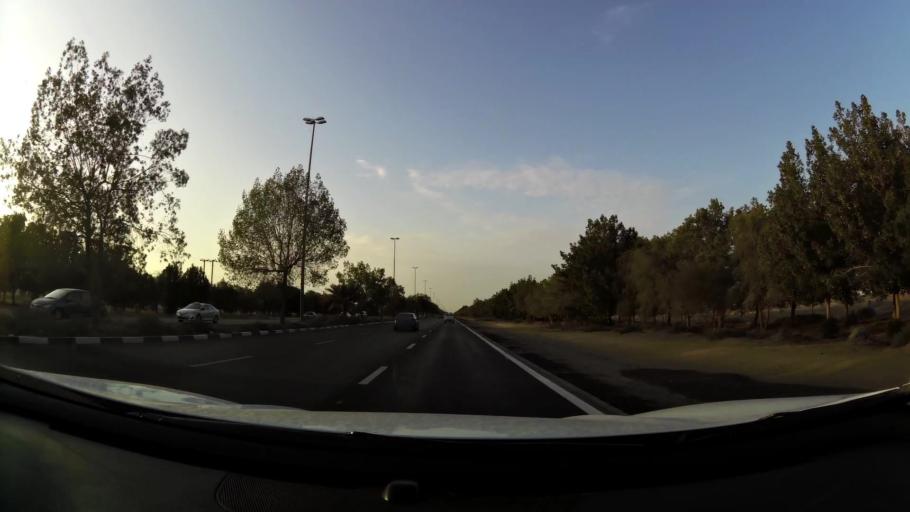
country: AE
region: Abu Dhabi
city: Al Ain
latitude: 24.1721
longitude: 55.7992
